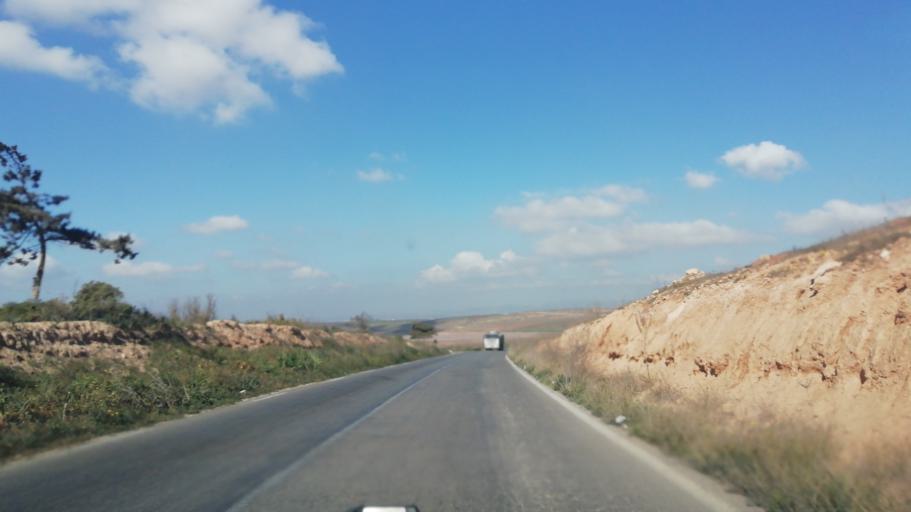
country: DZ
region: Oran
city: Ain el Bya
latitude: 35.7285
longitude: -0.2500
